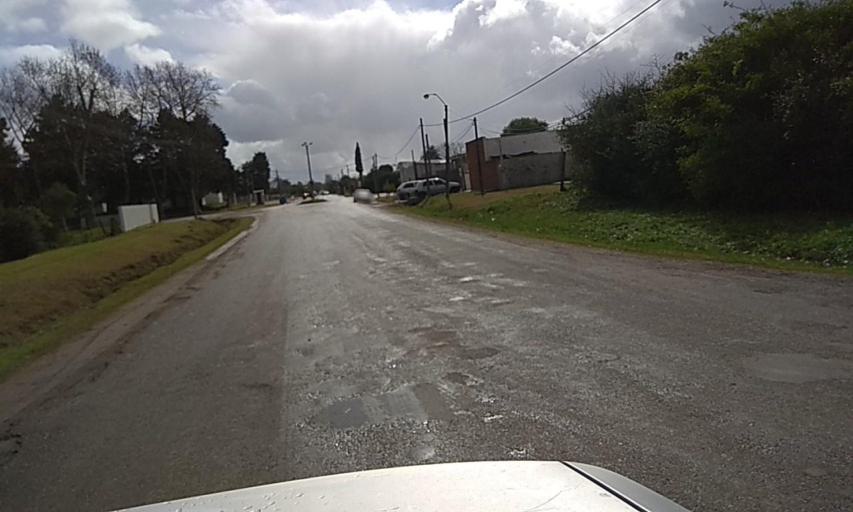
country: UY
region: Florida
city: Florida
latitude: -34.1056
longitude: -56.2240
